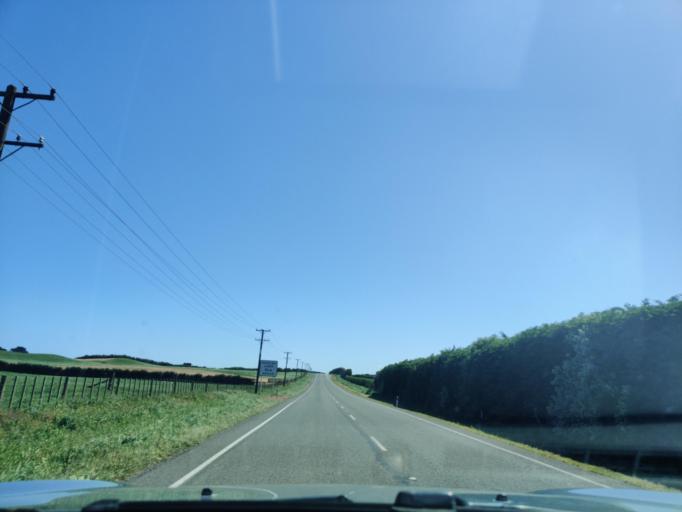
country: NZ
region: Taranaki
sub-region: South Taranaki District
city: Patea
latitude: -39.6996
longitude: 174.4349
